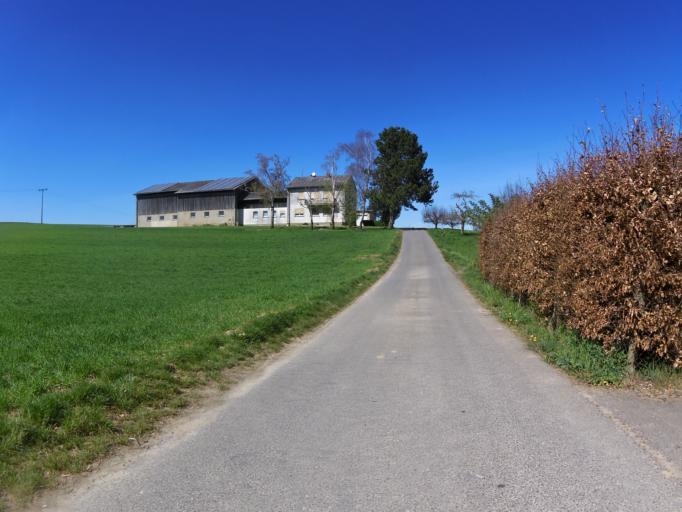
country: DE
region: Bavaria
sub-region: Regierungsbezirk Unterfranken
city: Biebelried
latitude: 49.7982
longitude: 10.1013
